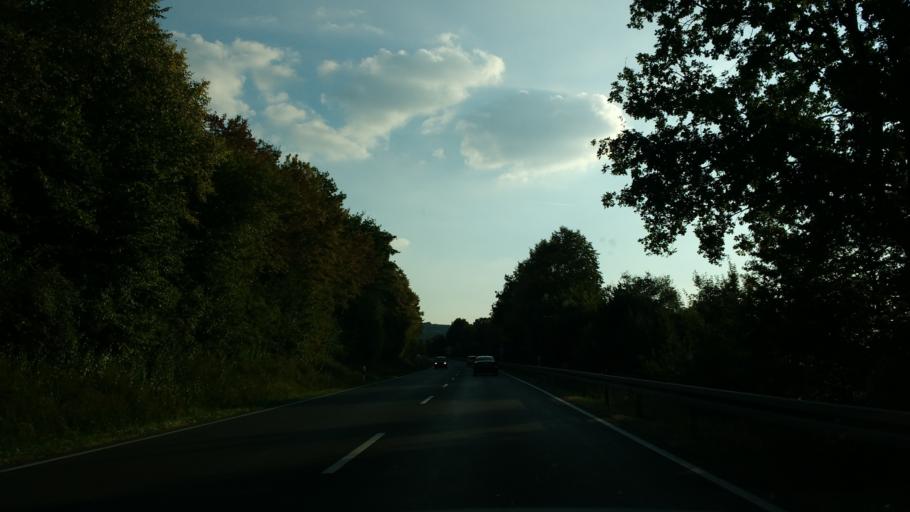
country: DE
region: Bavaria
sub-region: Regierungsbezirk Unterfranken
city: Fuchsstadt
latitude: 50.1165
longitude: 9.9406
